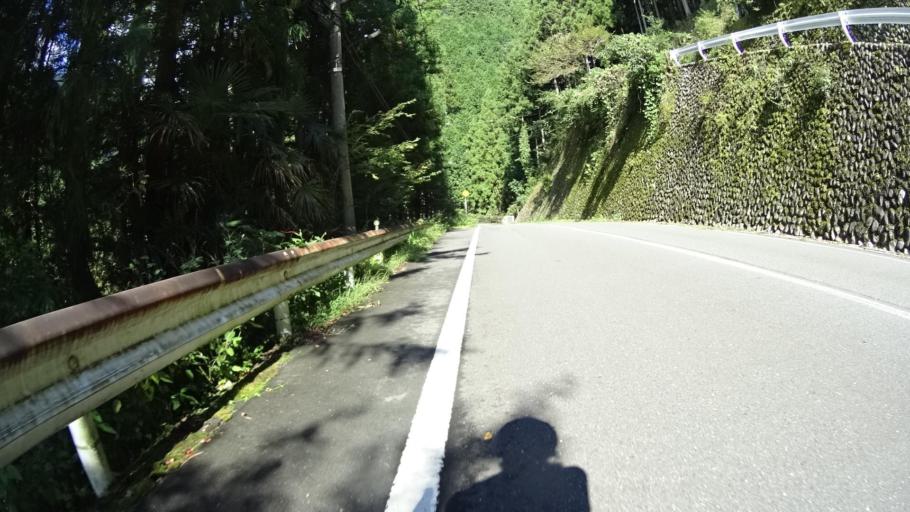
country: JP
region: Yamanashi
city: Uenohara
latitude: 35.7357
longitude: 139.0951
